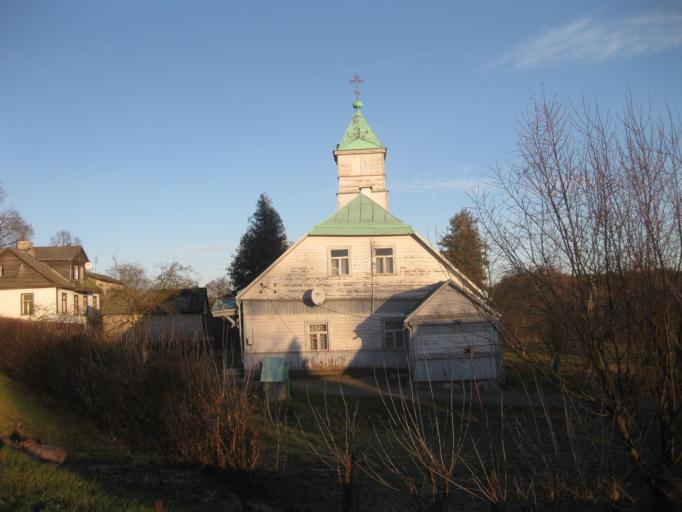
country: LT
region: Vilnius County
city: Ukmerge
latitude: 55.2489
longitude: 24.7684
